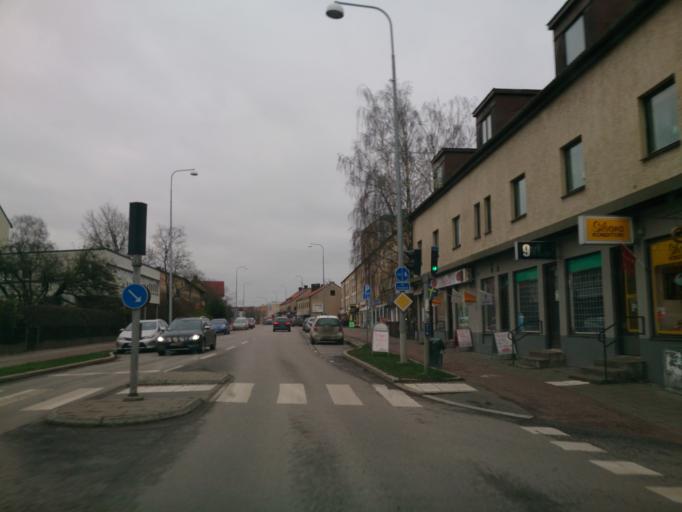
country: SE
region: OEstergoetland
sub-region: Linkopings Kommun
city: Linkoping
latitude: 58.4058
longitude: 15.6427
